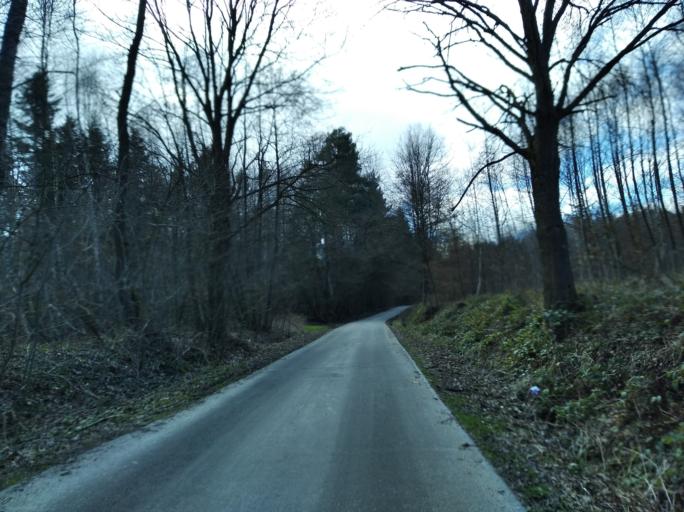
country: PL
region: Subcarpathian Voivodeship
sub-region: Powiat strzyzowski
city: Wysoka Strzyzowska
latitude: 49.8014
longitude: 21.7388
